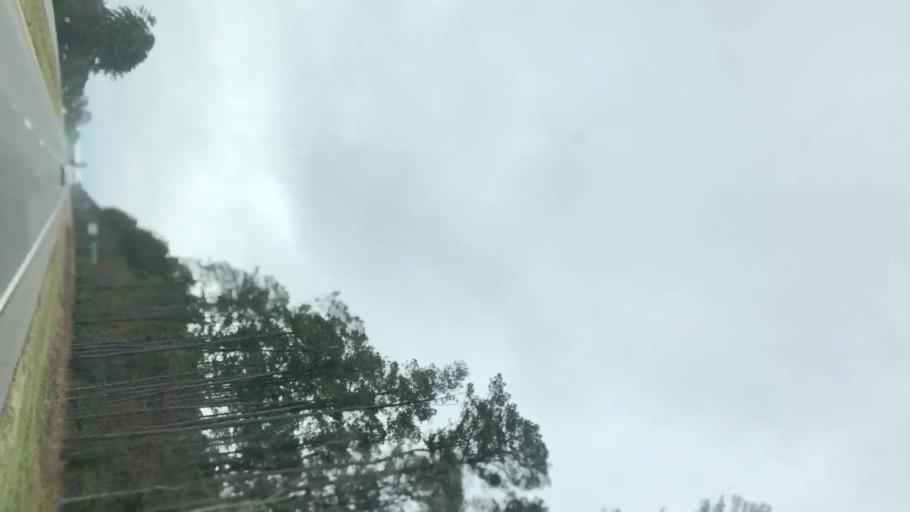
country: US
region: South Carolina
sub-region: Hampton County
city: Yemassee
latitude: 32.6834
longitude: -80.6358
